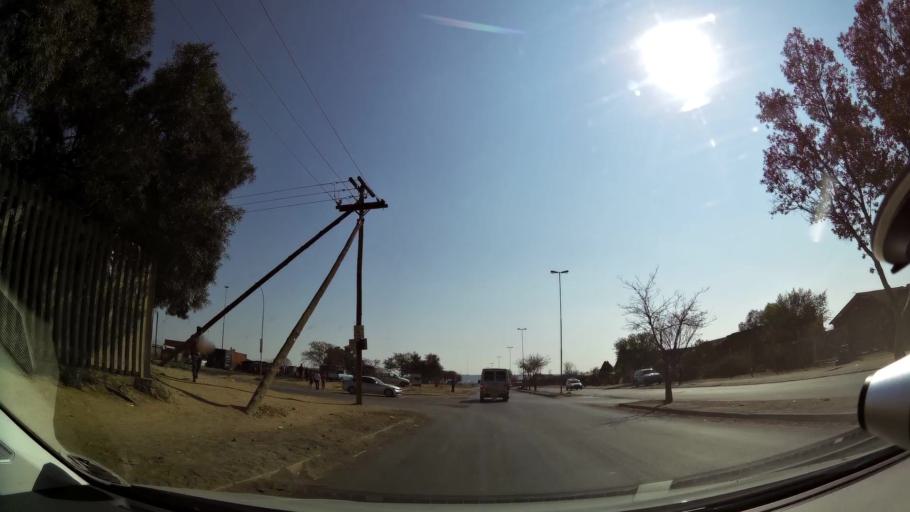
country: ZA
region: Orange Free State
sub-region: Mangaung Metropolitan Municipality
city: Bloemfontein
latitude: -29.1555
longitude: 26.2537
